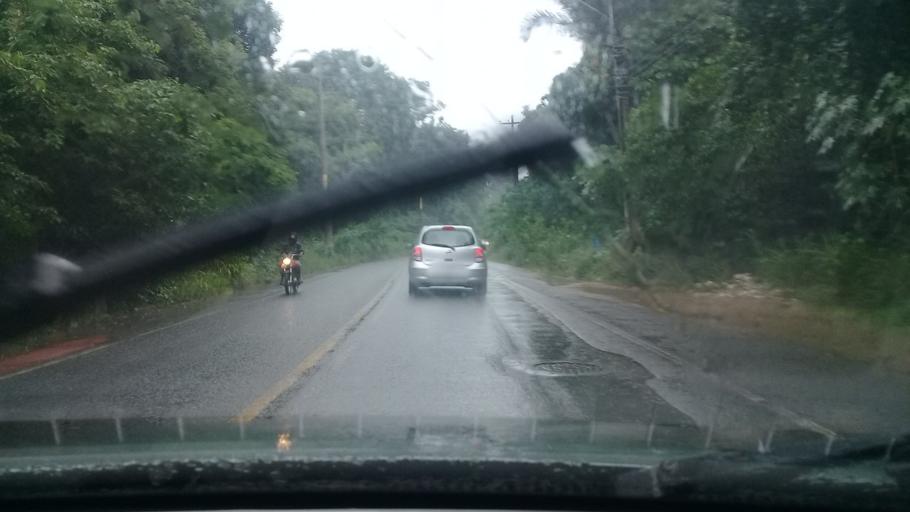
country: BR
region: Pernambuco
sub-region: Paulista
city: Paulista
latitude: -7.9473
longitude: -34.8816
